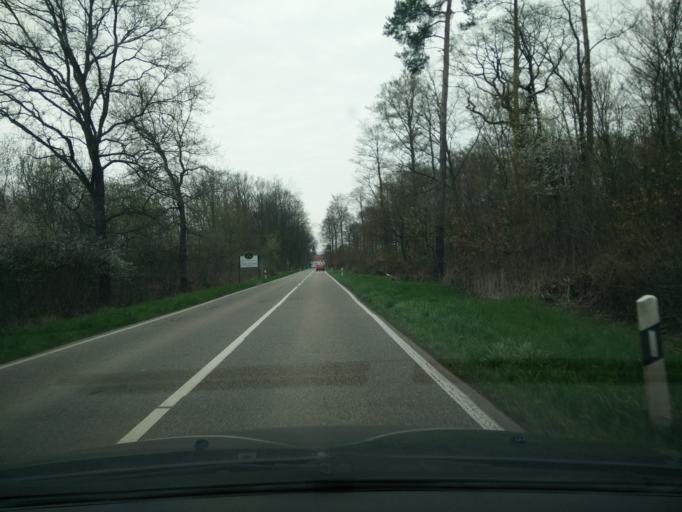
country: DE
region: Rheinland-Pfalz
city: Vollmersweiler
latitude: 49.0509
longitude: 8.0898
